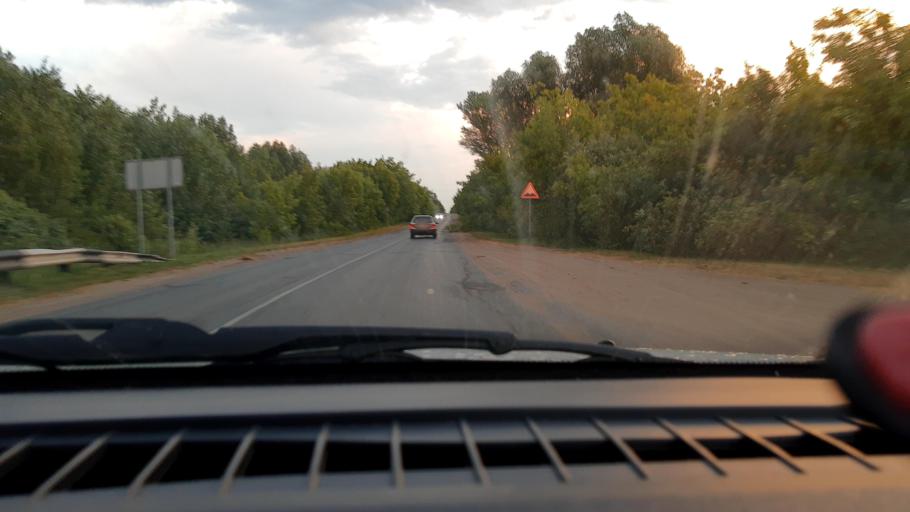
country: RU
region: Nizjnij Novgorod
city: Kstovo
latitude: 56.1353
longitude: 44.0913
